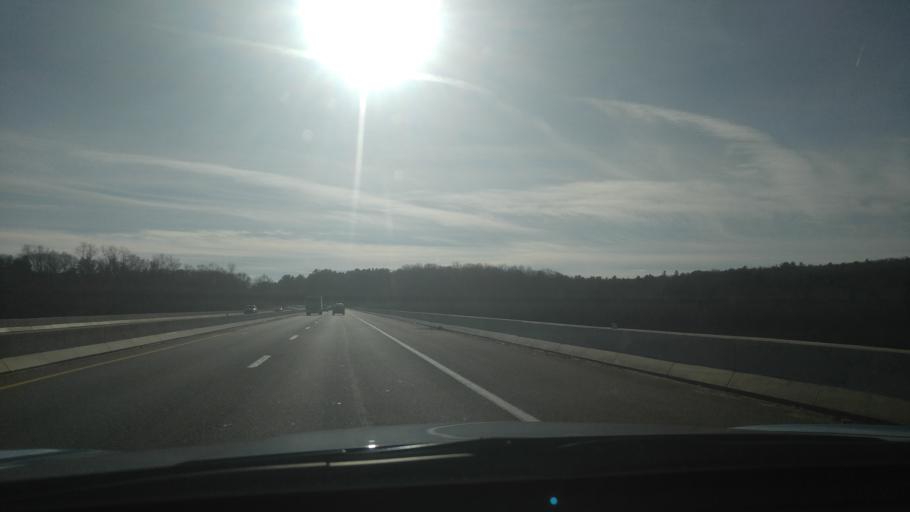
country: US
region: Rhode Island
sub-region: Providence County
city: Cumberland Hill
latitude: 41.9793
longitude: -71.4847
